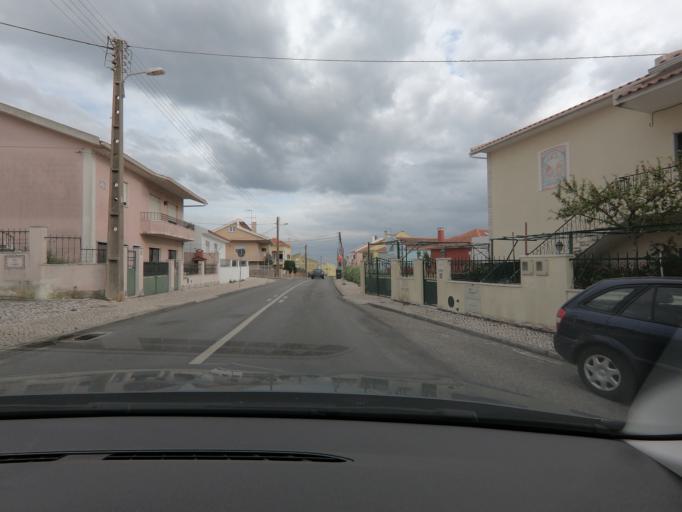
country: PT
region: Lisbon
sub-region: Cascais
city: Sao Domingos de Rana
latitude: 38.7149
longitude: -9.3326
